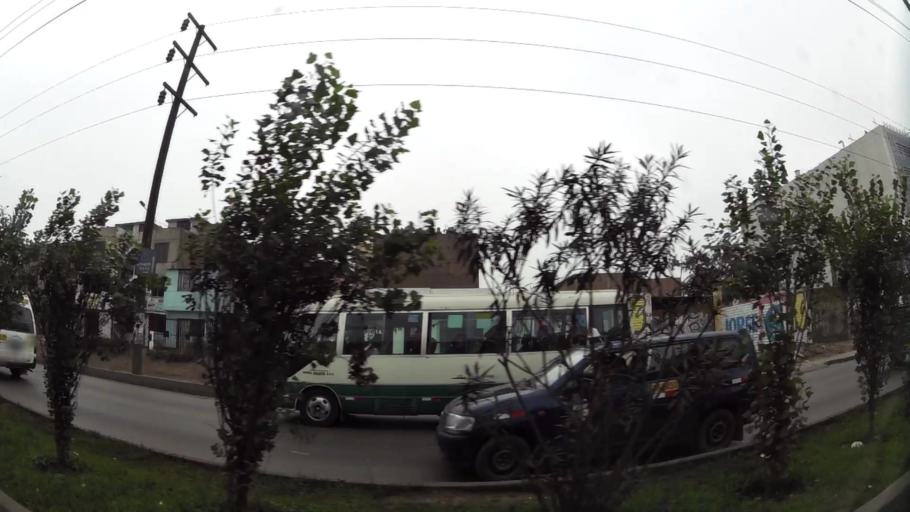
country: PE
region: Lima
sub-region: Lima
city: Vitarte
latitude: -12.0234
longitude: -76.9123
